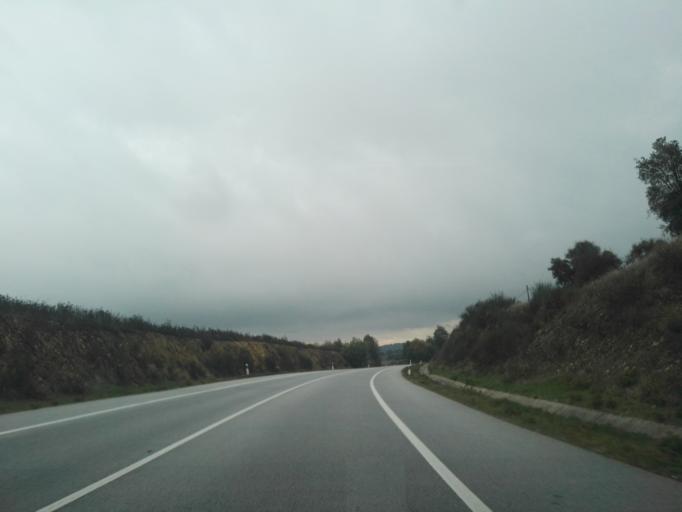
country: PT
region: Portalegre
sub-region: Portalegre
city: Urra
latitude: 39.2275
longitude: -7.3838
